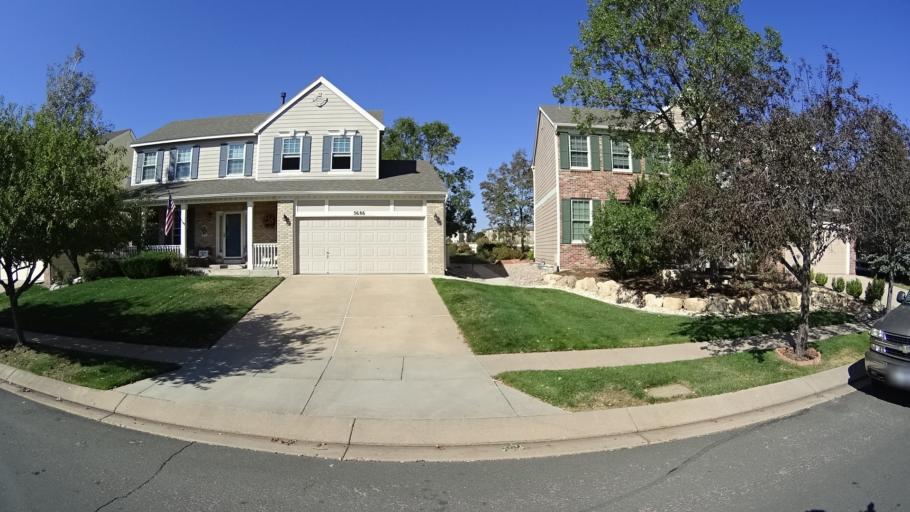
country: US
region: Colorado
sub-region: El Paso County
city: Cimarron Hills
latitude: 38.8845
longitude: -104.7089
